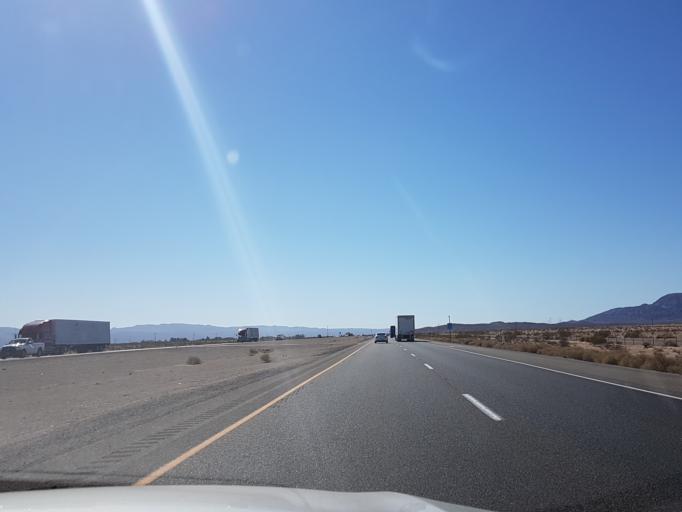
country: US
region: California
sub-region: San Bernardino County
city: Fort Irwin
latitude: 34.9443
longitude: -116.6890
